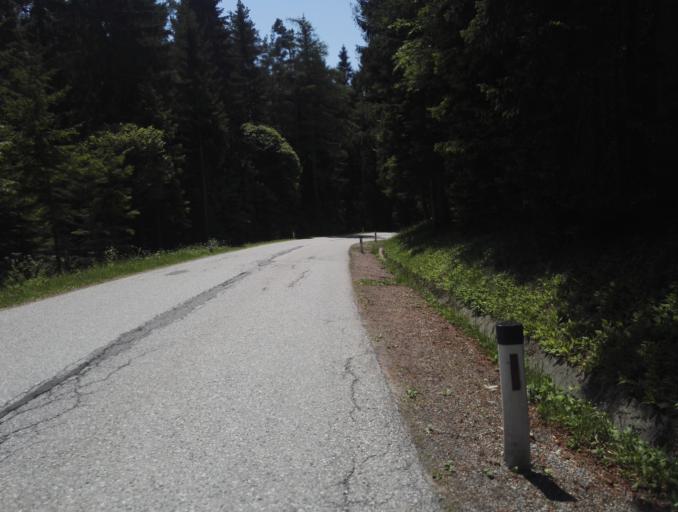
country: AT
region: Styria
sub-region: Politischer Bezirk Weiz
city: Stenzengreith
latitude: 47.2020
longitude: 15.4859
